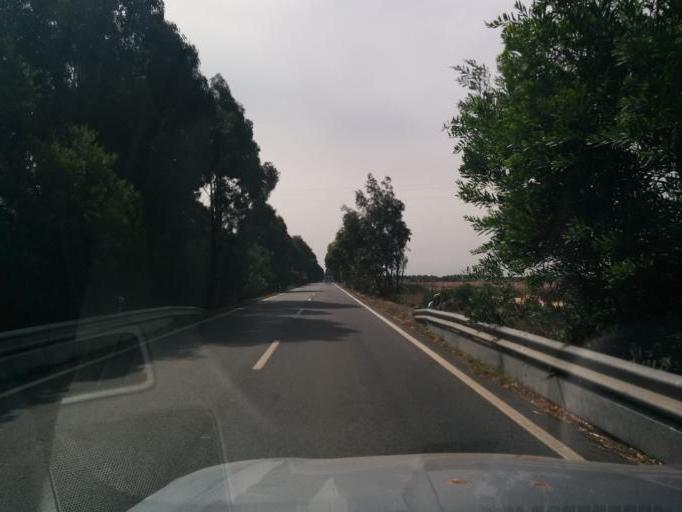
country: PT
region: Beja
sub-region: Odemira
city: Vila Nova de Milfontes
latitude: 37.6902
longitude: -8.7668
